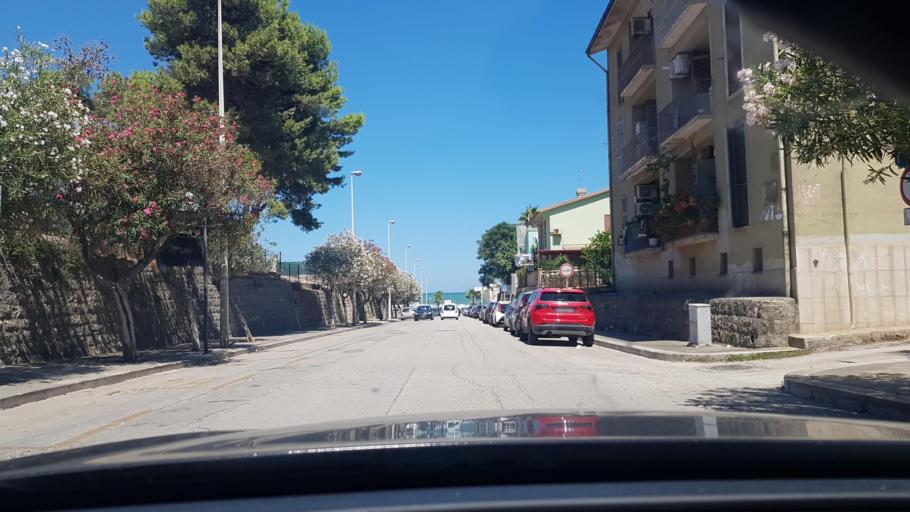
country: IT
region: Apulia
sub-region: Provincia di Barletta - Andria - Trani
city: Barletta
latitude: 41.3180
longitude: 16.2986
